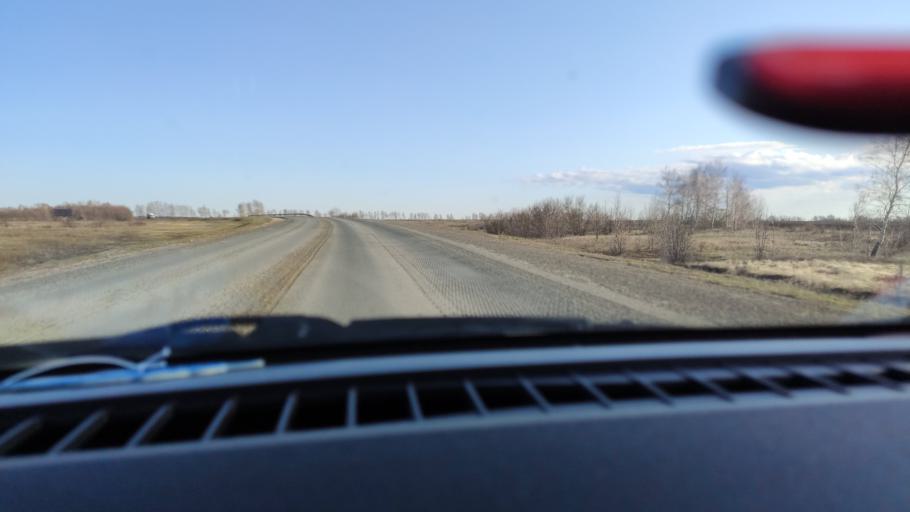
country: RU
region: Saratov
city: Dukhovnitskoye
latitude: 52.7130
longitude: 48.2667
